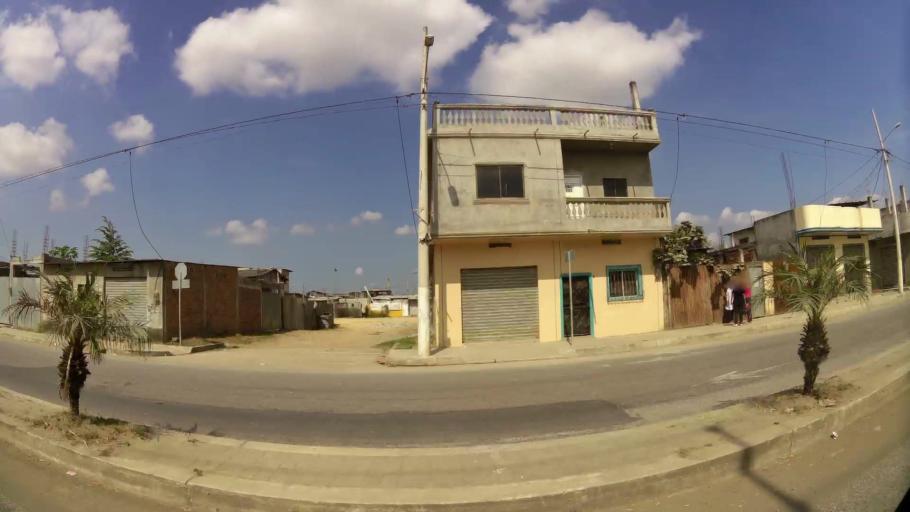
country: EC
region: Guayas
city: Eloy Alfaro
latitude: -2.1694
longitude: -79.8281
